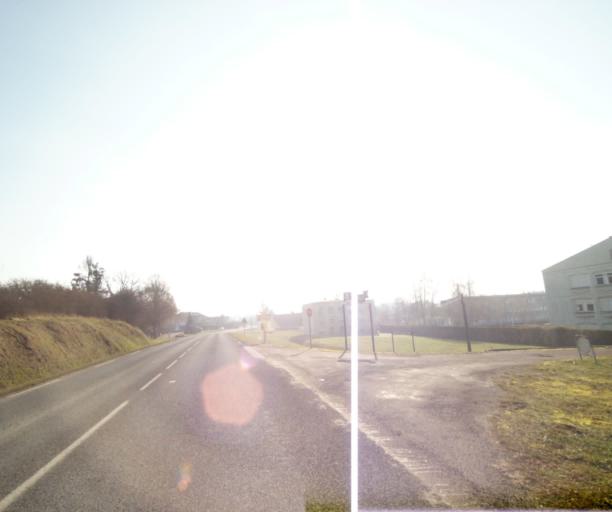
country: FR
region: Champagne-Ardenne
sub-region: Departement de la Haute-Marne
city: Wassy
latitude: 48.5063
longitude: 4.9421
